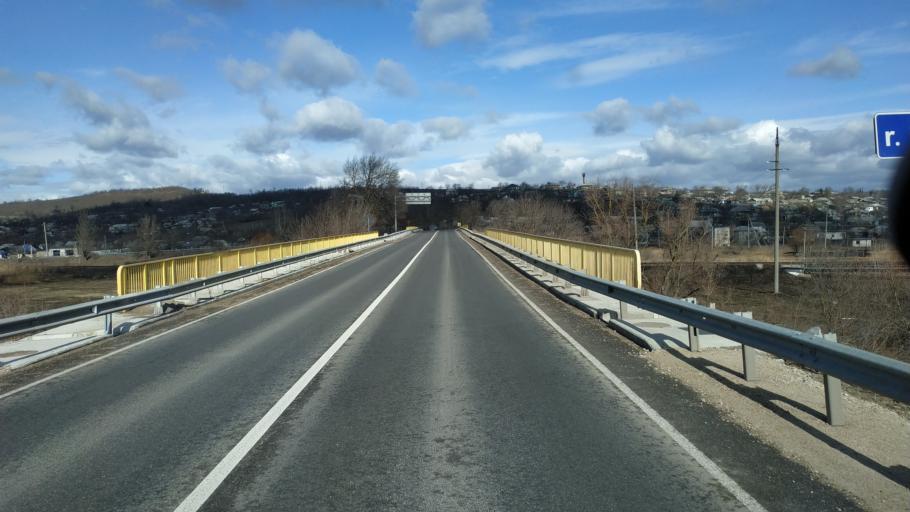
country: MD
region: Stinga Nistrului
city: Bucovat
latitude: 47.1835
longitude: 28.4670
